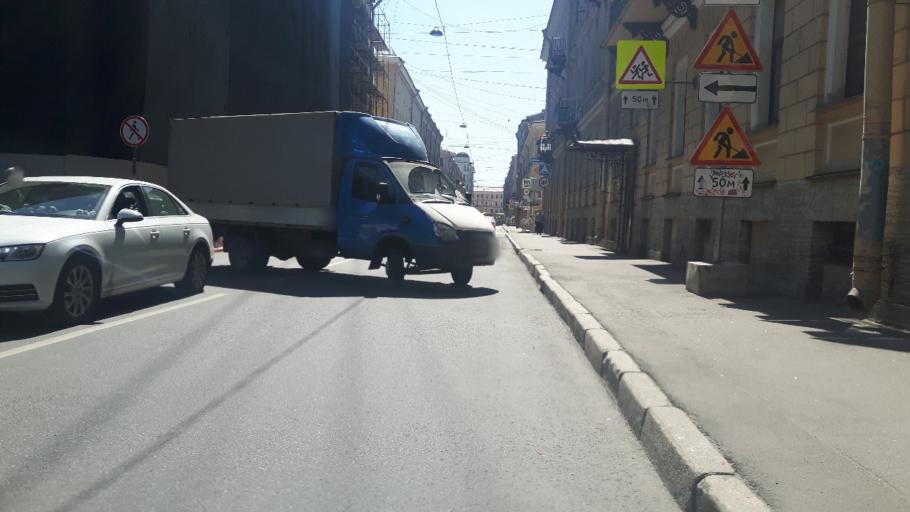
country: RU
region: St.-Petersburg
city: Saint Petersburg
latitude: 59.9300
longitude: 30.3043
